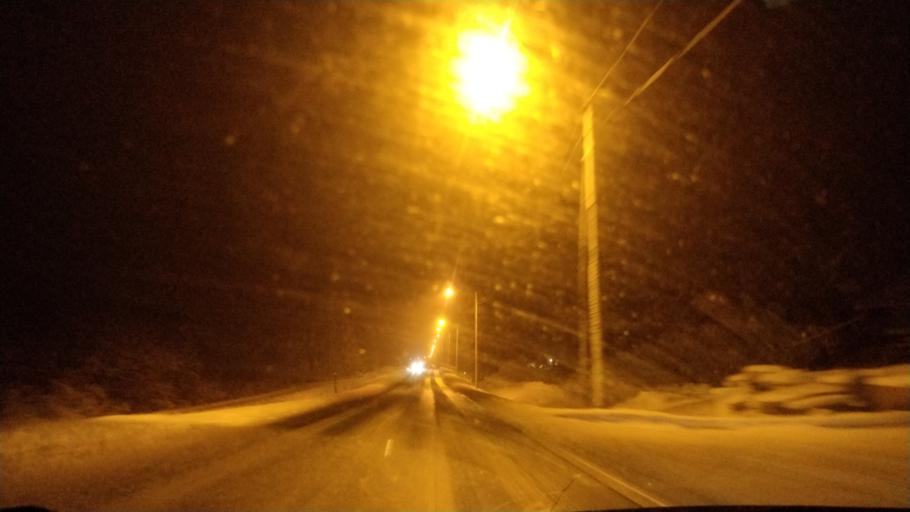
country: FI
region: Lapland
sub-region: Rovaniemi
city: Rovaniemi
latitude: 66.4102
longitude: 25.4029
